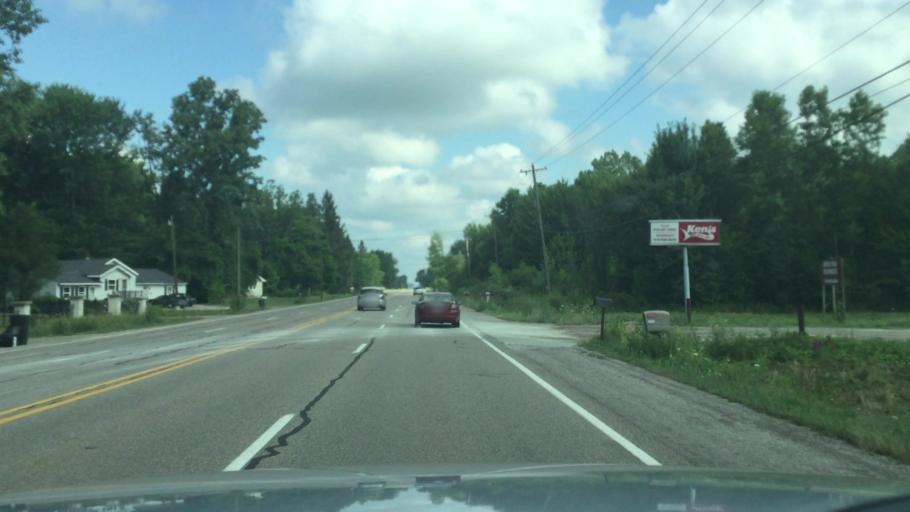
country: US
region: Michigan
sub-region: Genesee County
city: Clio
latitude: 43.2160
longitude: -83.7435
